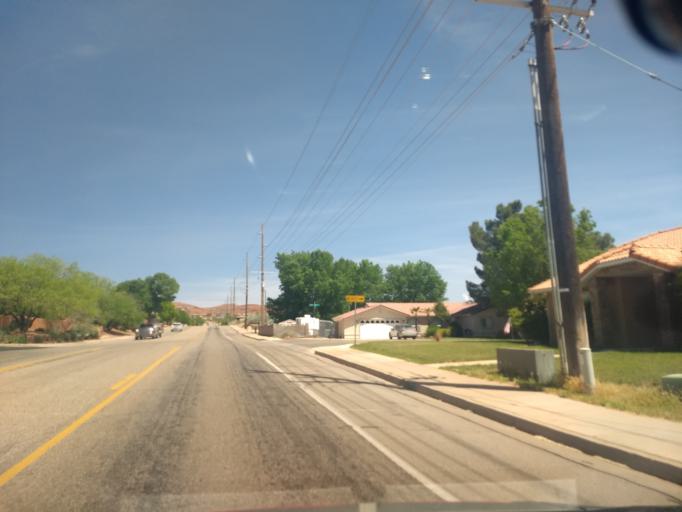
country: US
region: Utah
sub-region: Washington County
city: Santa Clara
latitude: 37.1429
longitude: -113.6339
